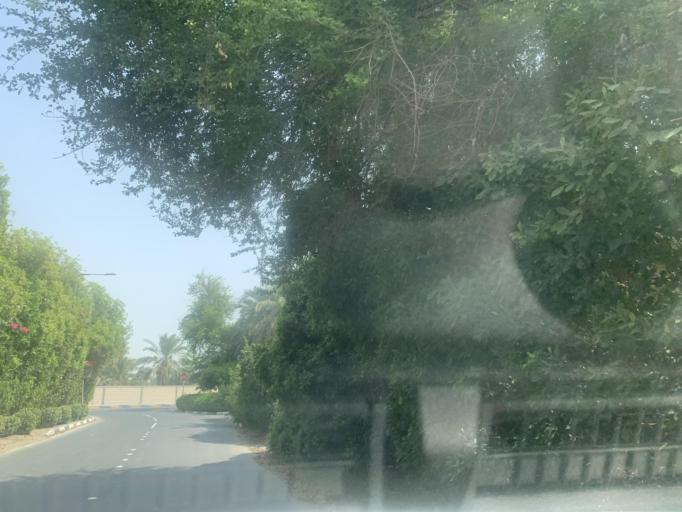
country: BH
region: Central Governorate
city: Madinat Hamad
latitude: 26.1673
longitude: 50.4535
